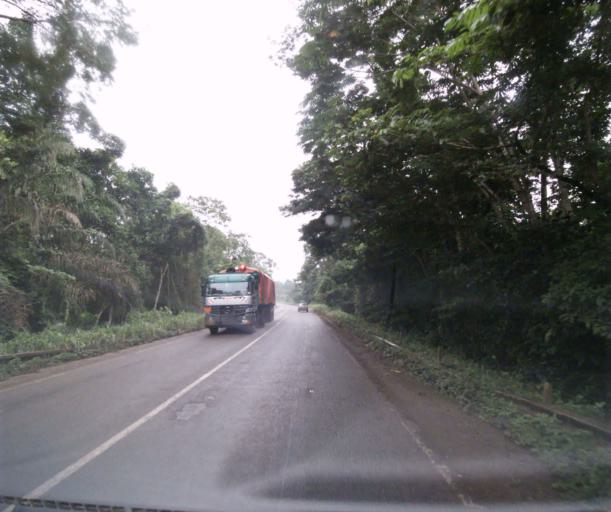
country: CM
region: Centre
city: Eseka
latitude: 3.8929
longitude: 10.7237
